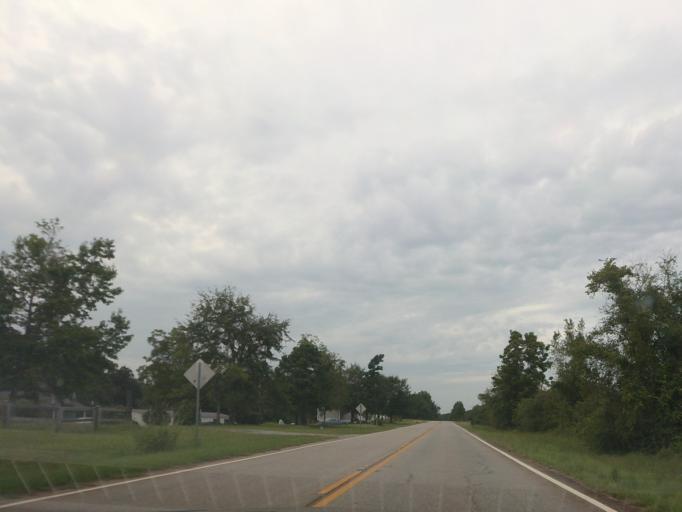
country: US
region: Georgia
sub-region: Twiggs County
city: Jeffersonville
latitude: 32.7266
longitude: -83.4175
